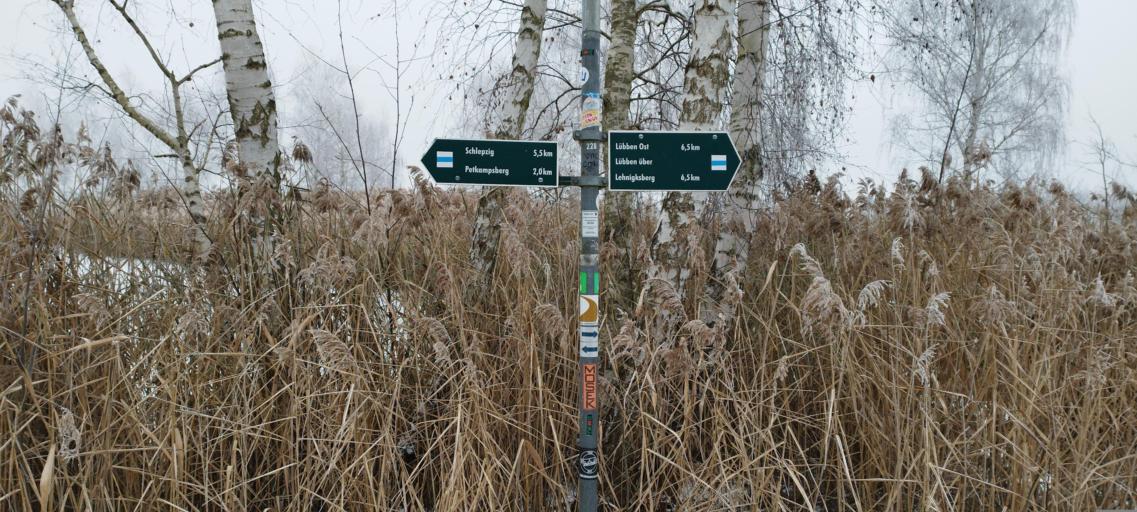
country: DE
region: Brandenburg
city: Schlepzig
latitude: 51.9922
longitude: 13.8869
